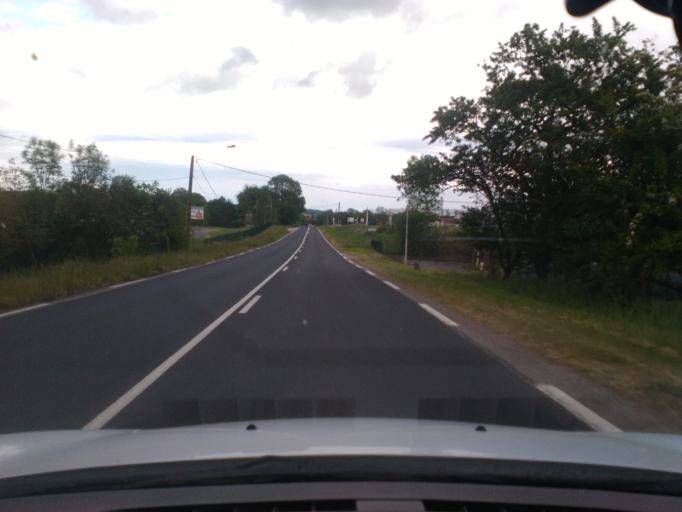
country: FR
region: Lorraine
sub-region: Departement des Vosges
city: Mirecourt
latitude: 48.3071
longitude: 6.1163
